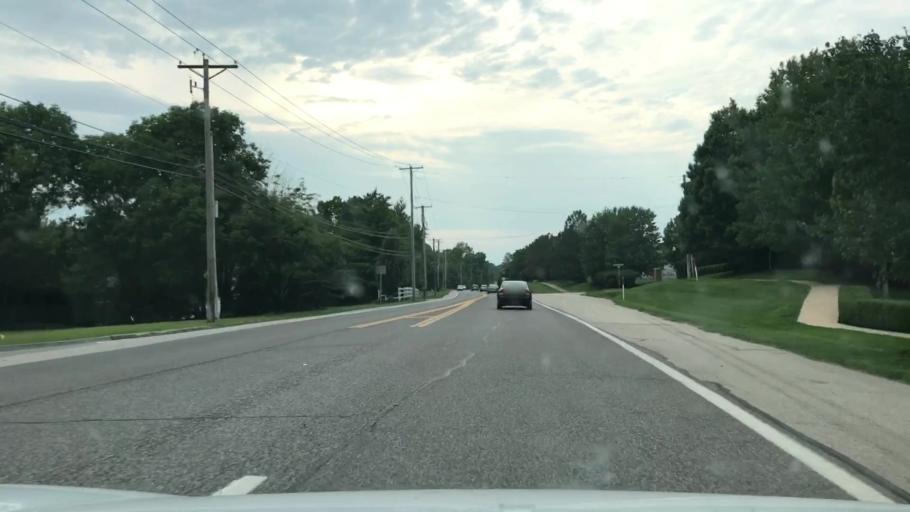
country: US
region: Missouri
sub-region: Saint Louis County
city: Chesterfield
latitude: 38.6561
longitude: -90.6112
